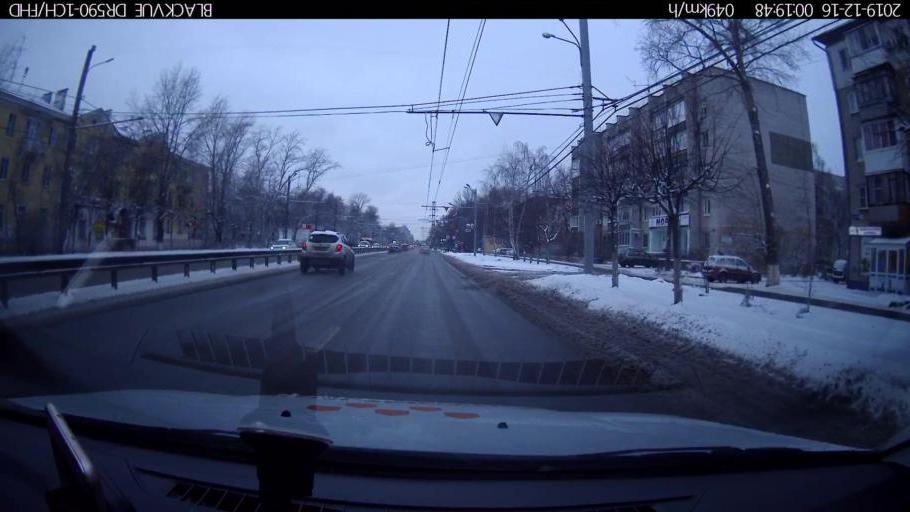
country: RU
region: Nizjnij Novgorod
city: Nizhniy Novgorod
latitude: 56.3183
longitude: 43.8925
